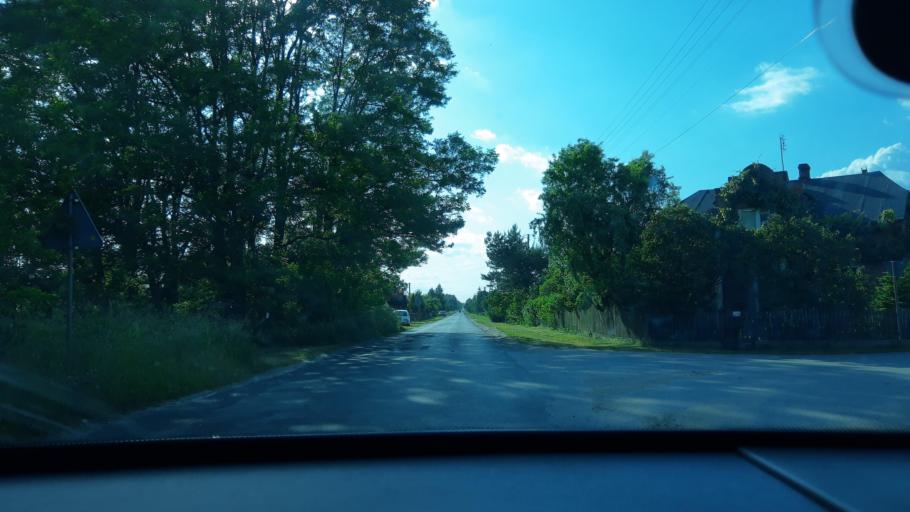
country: PL
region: Lodz Voivodeship
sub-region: Powiat zdunskowolski
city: Zapolice
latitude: 51.5386
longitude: 18.8071
